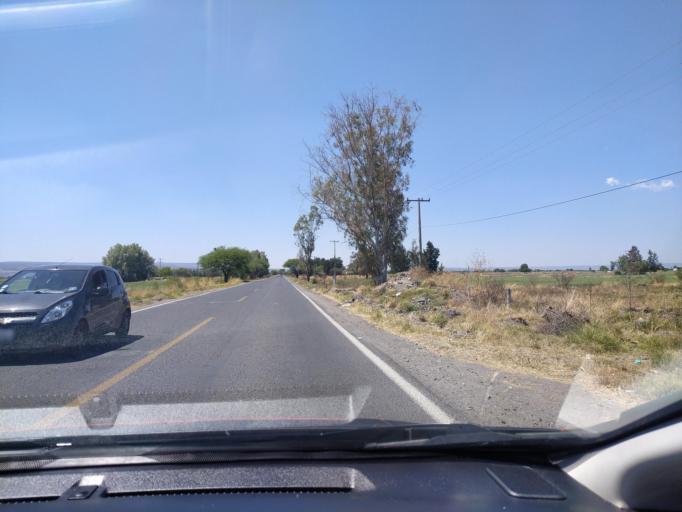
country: MX
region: Guanajuato
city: Ciudad Manuel Doblado
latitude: 20.7425
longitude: -101.8890
